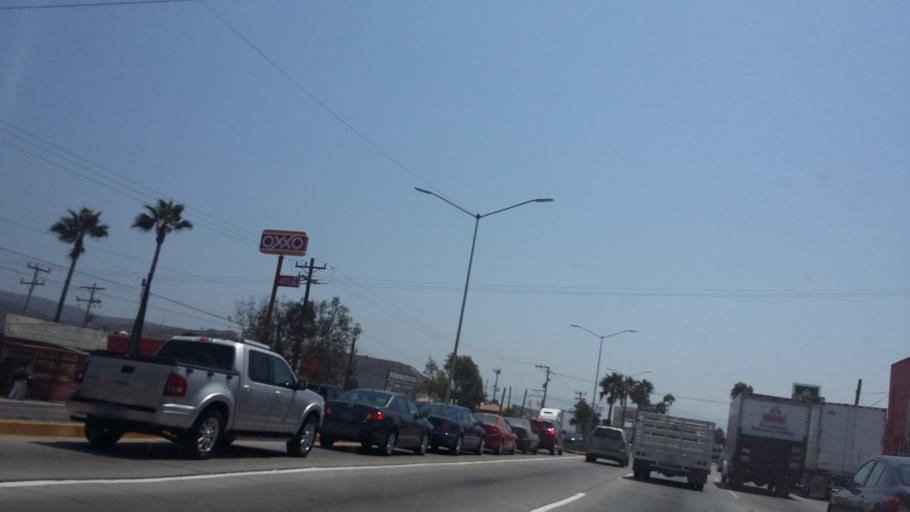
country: MX
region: Baja California
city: Ensenada
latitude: 31.8340
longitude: -116.6015
